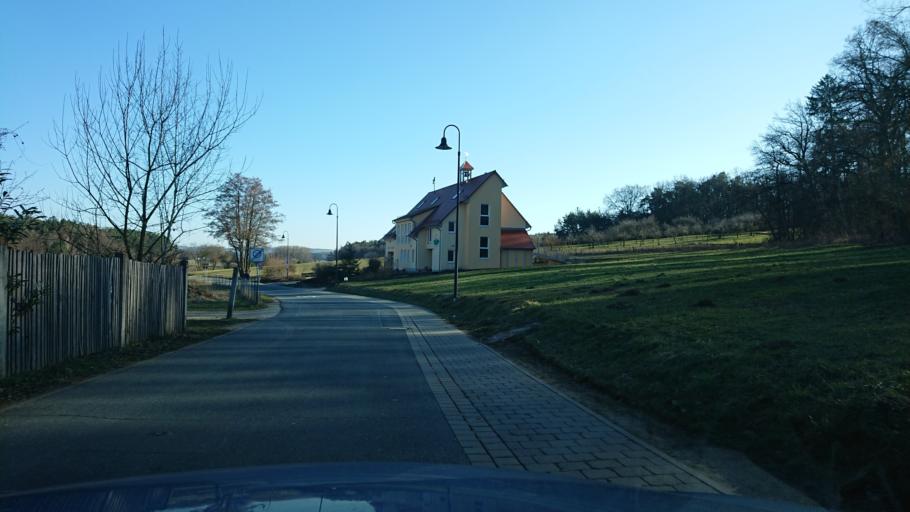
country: DE
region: Bavaria
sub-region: Upper Franconia
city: Neunkirchen am Brand
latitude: 49.6234
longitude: 11.1075
